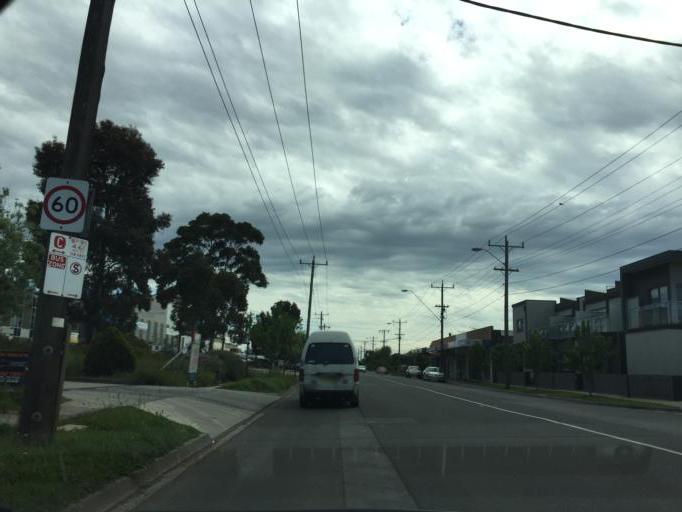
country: AU
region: Victoria
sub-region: Maribyrnong
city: Braybrook
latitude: -37.7915
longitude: 144.8635
